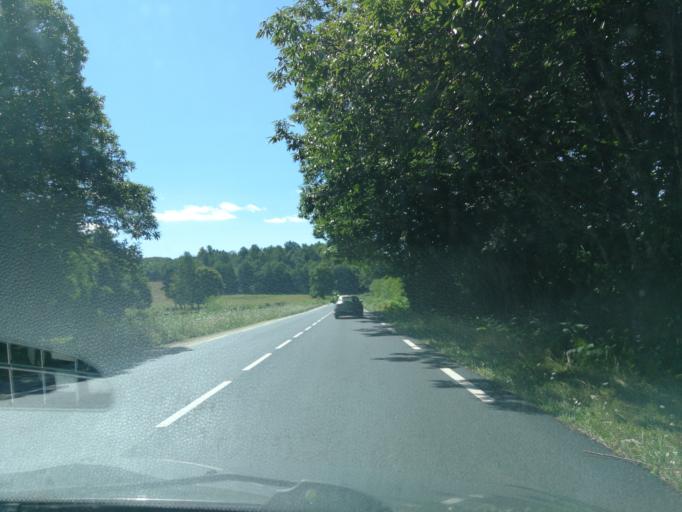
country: FR
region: Limousin
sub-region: Departement de la Correze
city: Sainte-Fortunade
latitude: 45.1686
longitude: 1.7570
